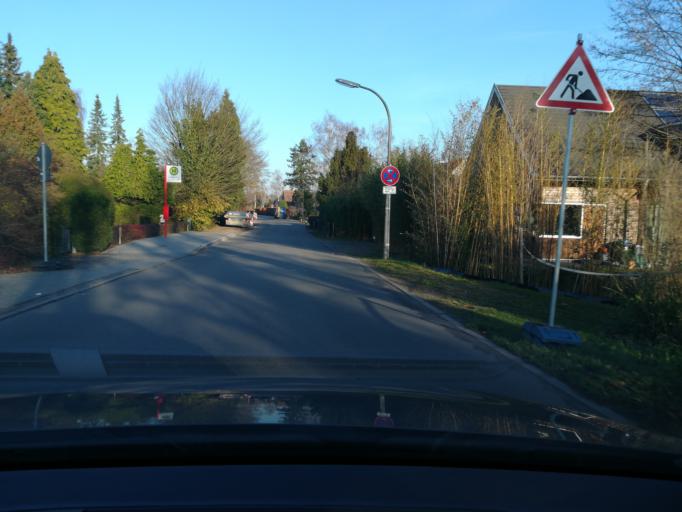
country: DE
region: Lower Saxony
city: Stelle
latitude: 53.4410
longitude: 10.1213
